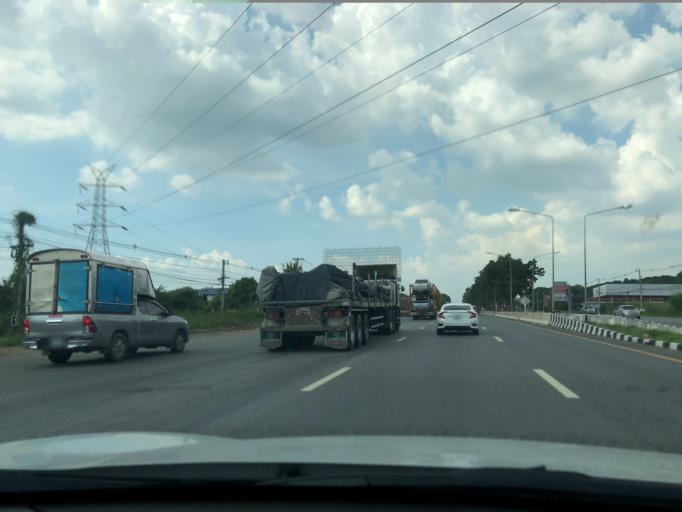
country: TH
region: Nakhon Sawan
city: Krok Phra
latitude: 15.5895
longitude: 100.1235
